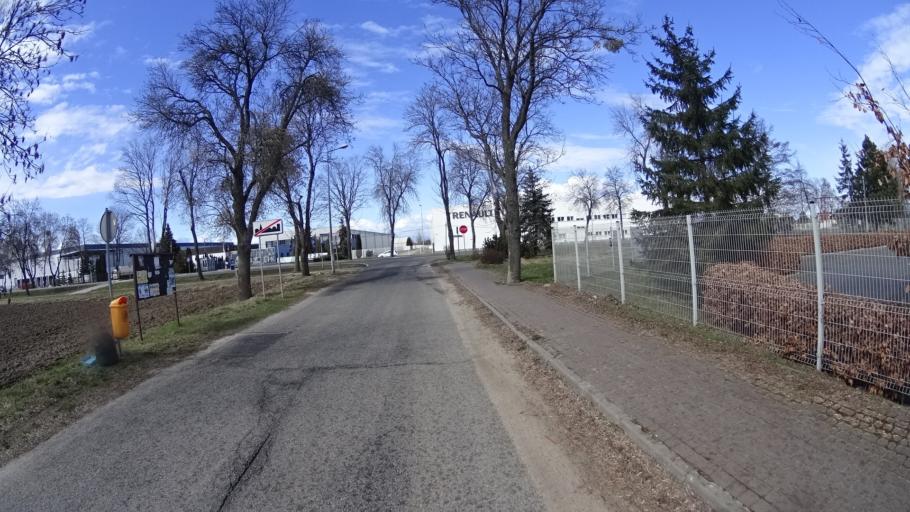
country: PL
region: Masovian Voivodeship
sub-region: Powiat warszawski zachodni
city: Jozefow
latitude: 52.2106
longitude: 20.6821
